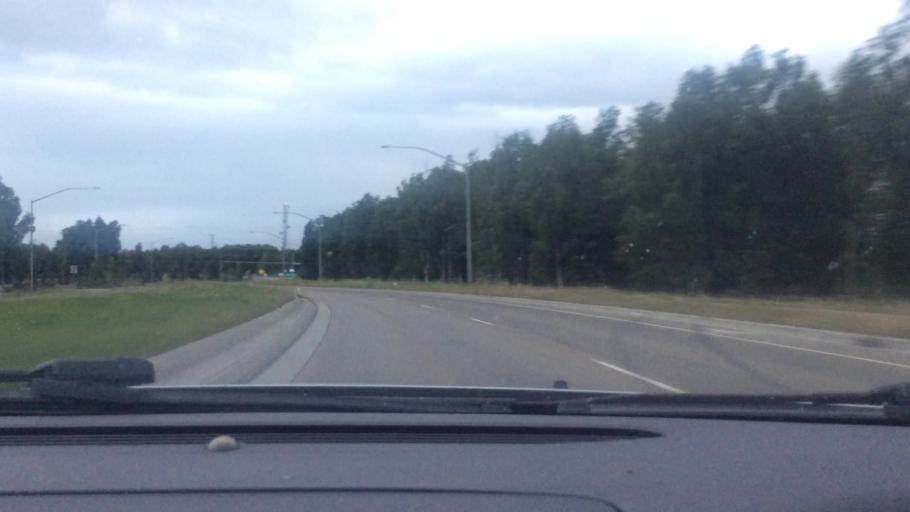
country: US
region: Alaska
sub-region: Anchorage Municipality
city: Anchorage
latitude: 61.1784
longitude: -149.8010
